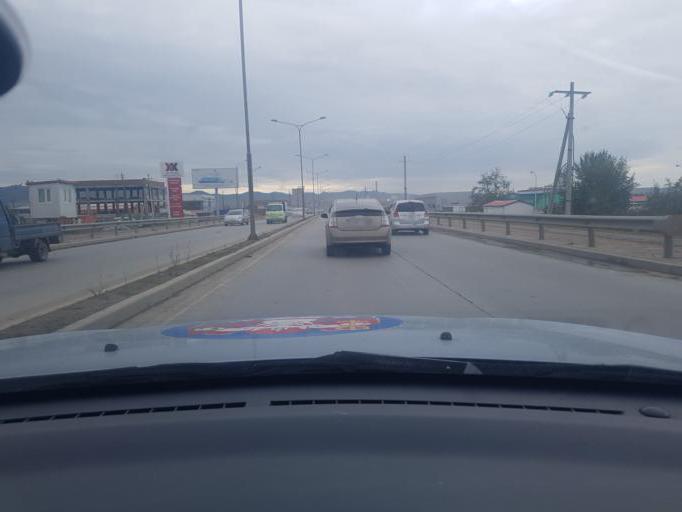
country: MN
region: Ulaanbaatar
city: Ulaanbaatar
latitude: 47.9003
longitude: 106.7857
